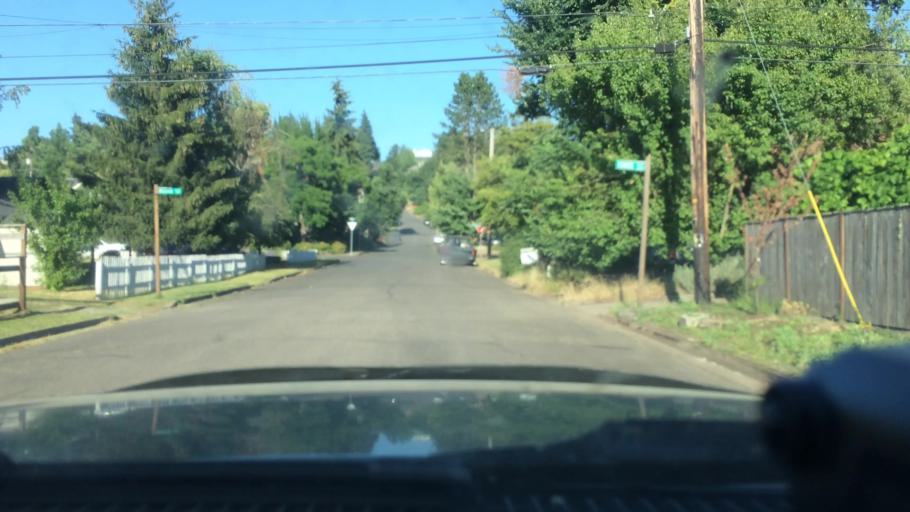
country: US
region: Oregon
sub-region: Lane County
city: Eugene
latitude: 44.0298
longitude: -123.1051
